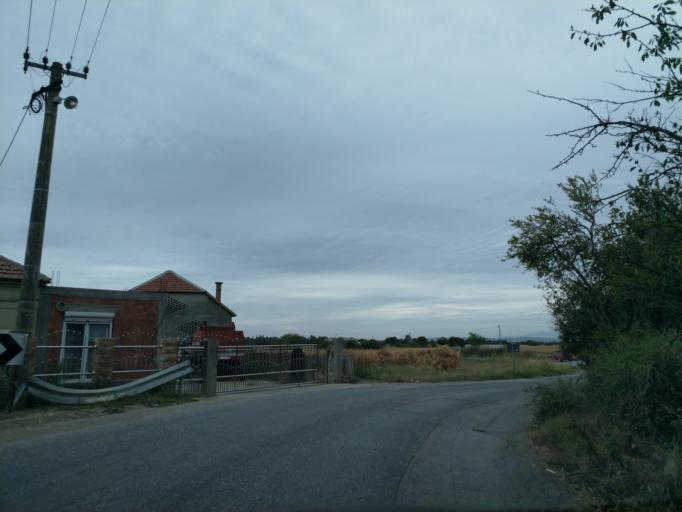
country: RS
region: Central Serbia
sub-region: Pomoravski Okrug
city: Paracin
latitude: 43.8347
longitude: 21.3279
